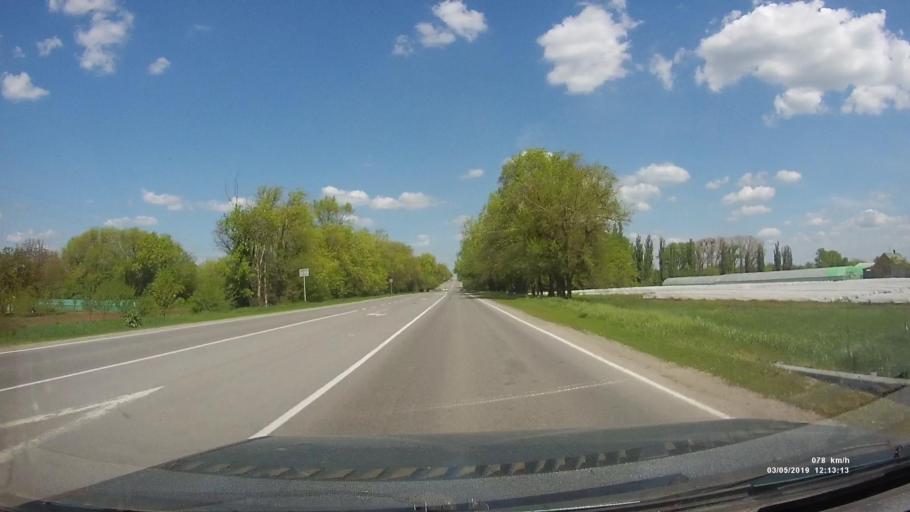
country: RU
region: Rostov
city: Melikhovskaya
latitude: 47.3305
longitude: 40.5533
